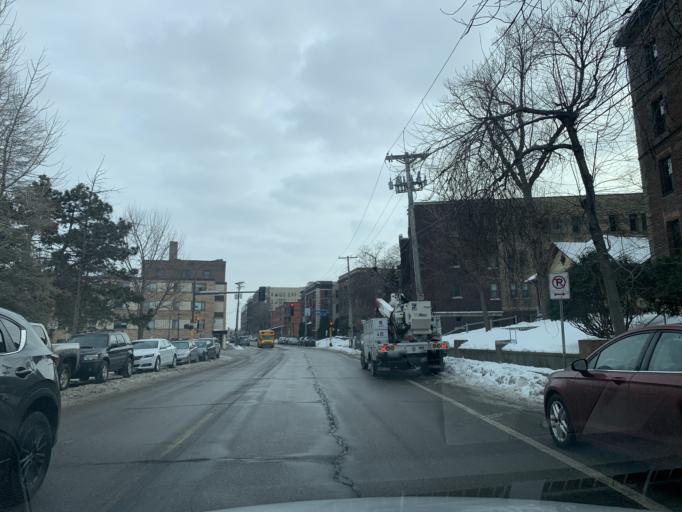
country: US
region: Minnesota
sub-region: Hennepin County
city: Minneapolis
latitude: 44.9679
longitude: -93.2829
